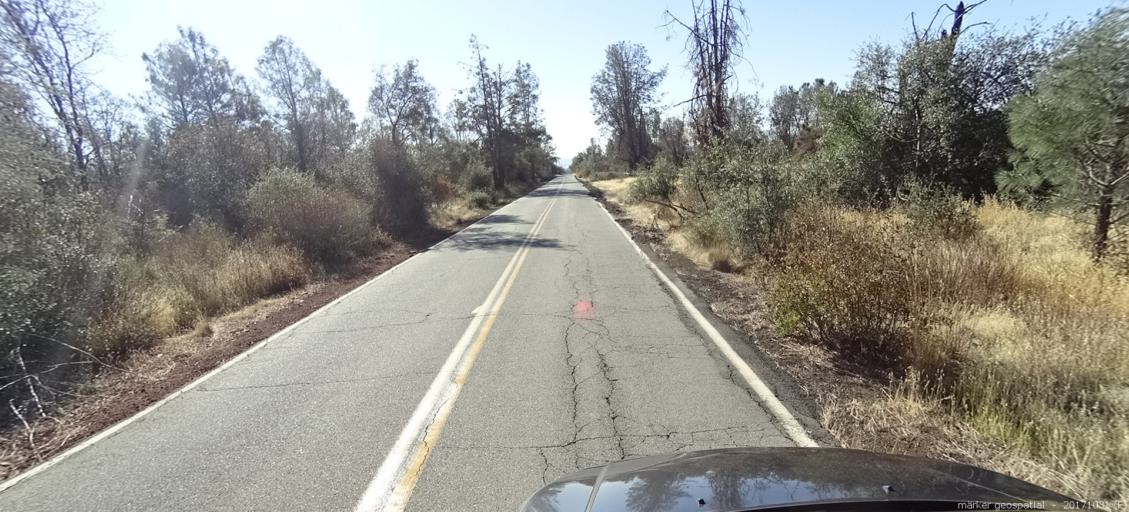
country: US
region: California
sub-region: Shasta County
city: Shingletown
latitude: 40.4487
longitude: -121.8994
